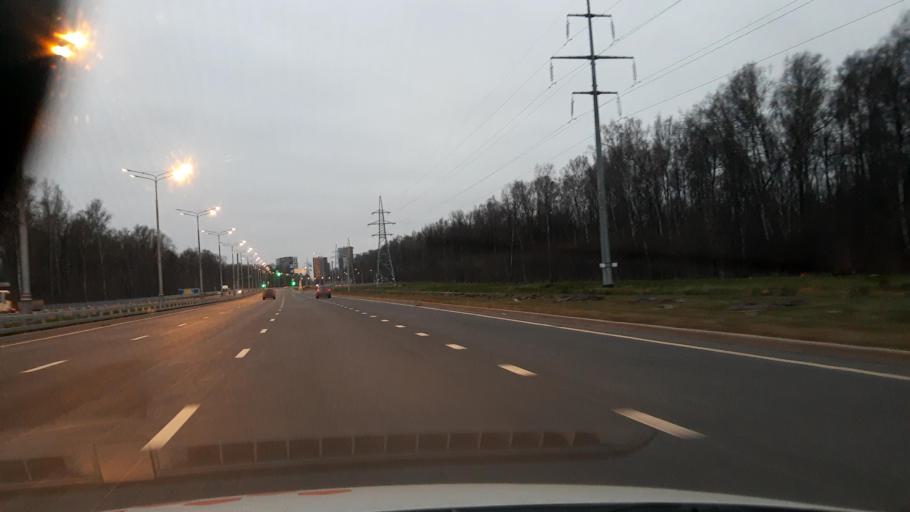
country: RU
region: Moskovskaya
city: Kommunarka
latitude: 55.5906
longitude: 37.4812
